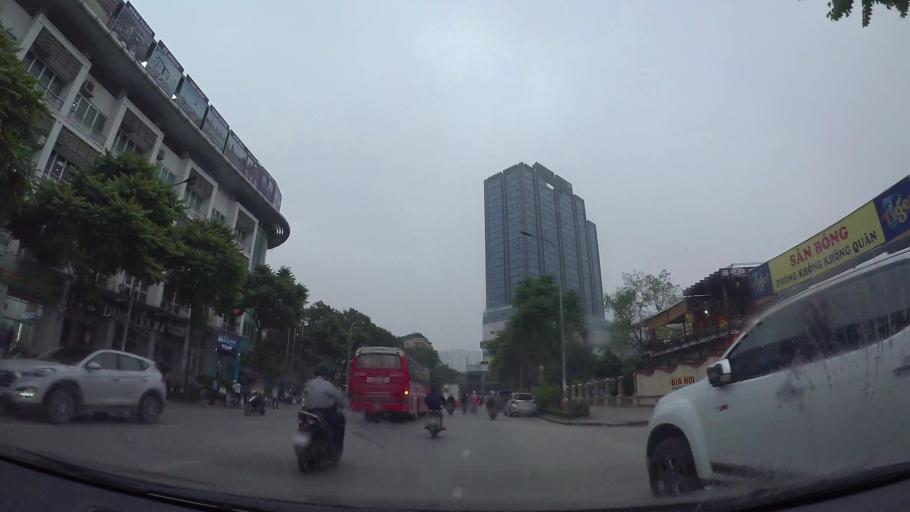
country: VN
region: Ha Noi
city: Dong Da
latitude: 20.9980
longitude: 105.8290
